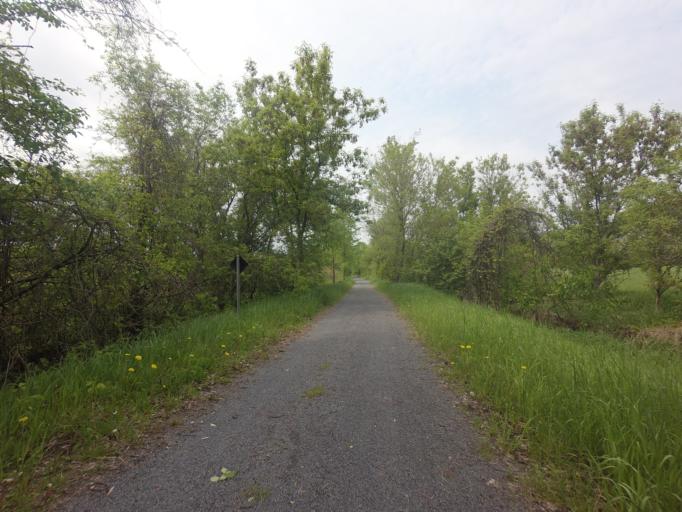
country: CA
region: Ontario
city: Kingston
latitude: 44.3651
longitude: -76.6270
